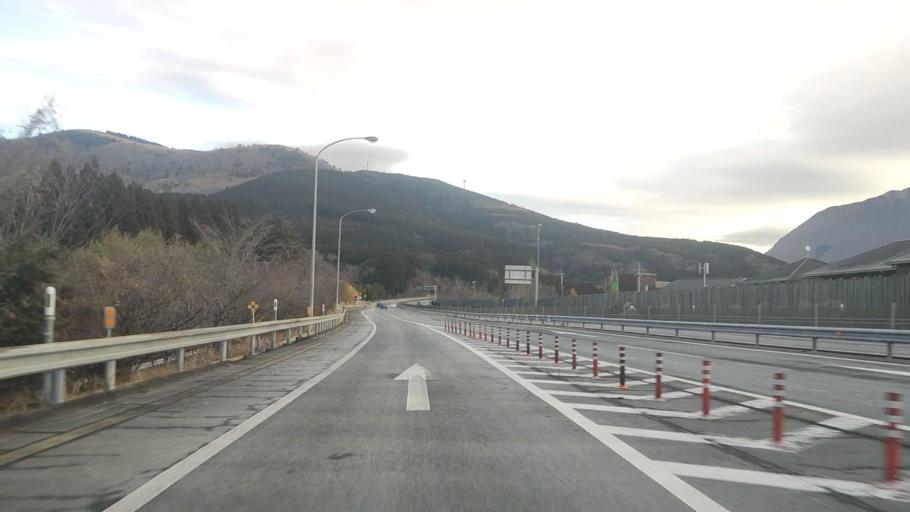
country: JP
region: Oita
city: Beppu
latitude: 33.2594
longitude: 131.3305
